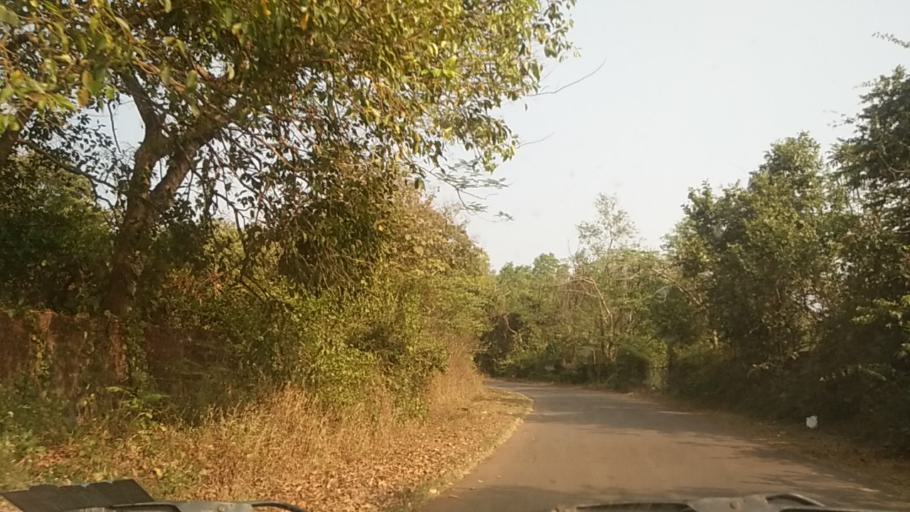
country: IN
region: Goa
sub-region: South Goa
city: Raia
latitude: 15.3166
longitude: 73.9516
